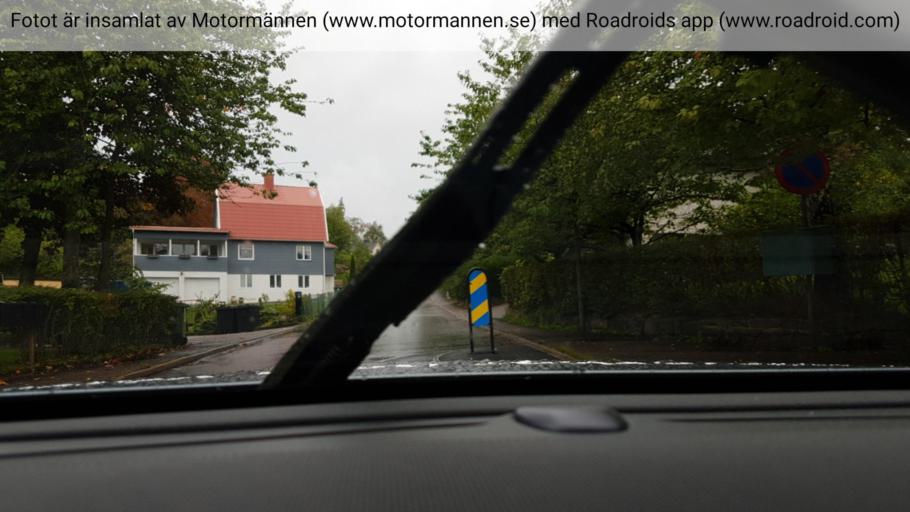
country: SE
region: Vaestra Goetaland
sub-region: Molndal
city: Moelndal
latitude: 57.6734
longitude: 11.9960
